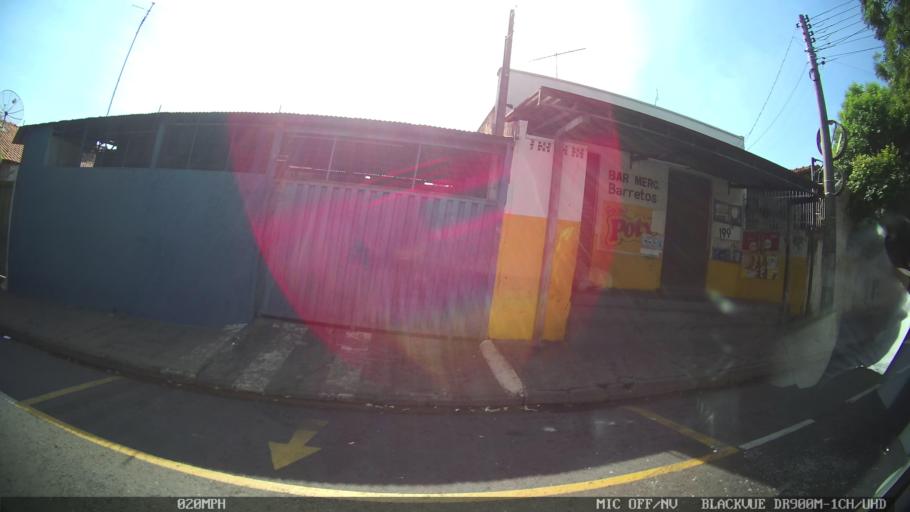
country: BR
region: Sao Paulo
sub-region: Sao Jose Do Rio Preto
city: Sao Jose do Rio Preto
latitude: -20.7952
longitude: -49.4229
